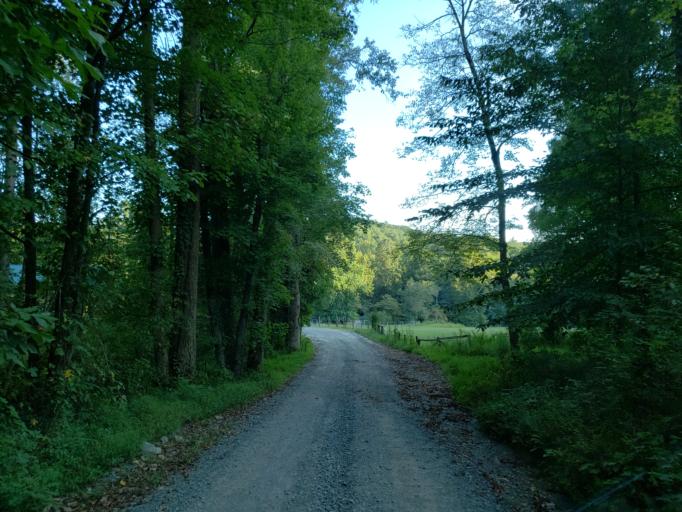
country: US
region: Georgia
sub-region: Fannin County
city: Blue Ridge
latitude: 34.6862
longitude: -84.2682
